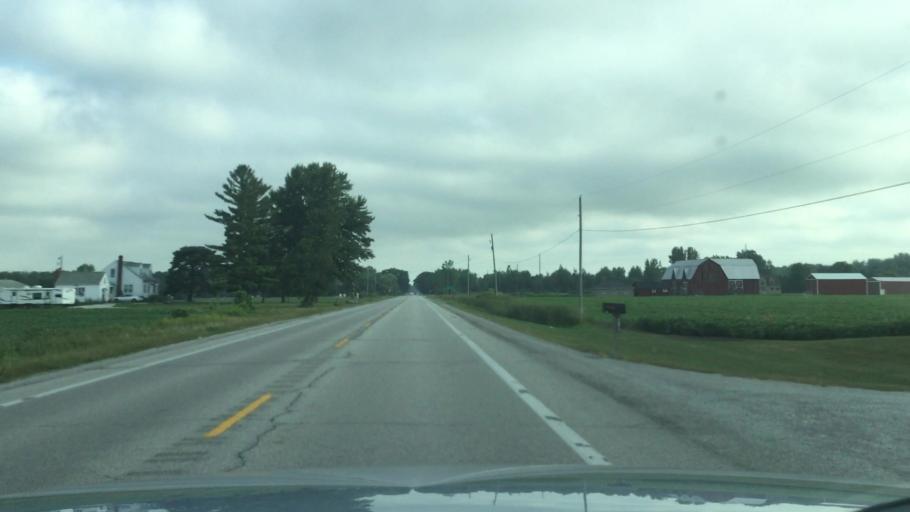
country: US
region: Michigan
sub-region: Saginaw County
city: Birch Run
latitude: 43.2605
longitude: -83.7356
